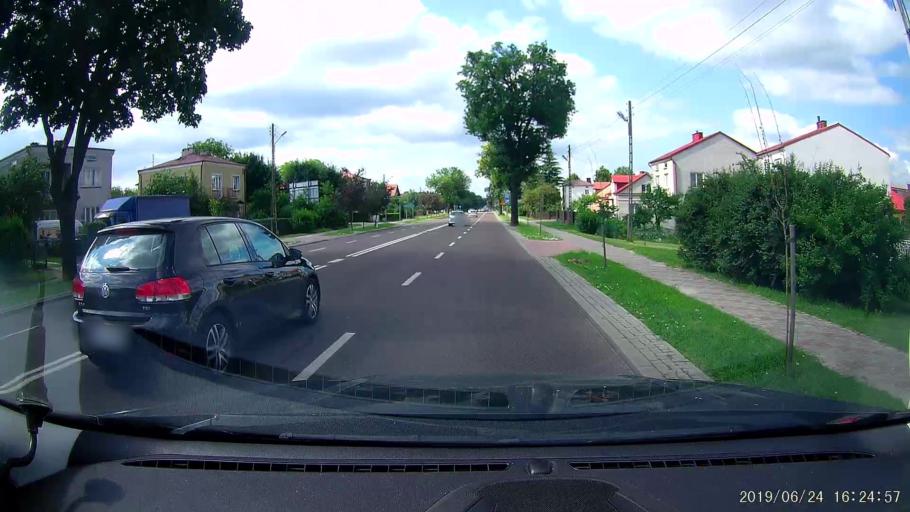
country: PL
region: Lublin Voivodeship
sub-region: Powiat tomaszowski
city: Tomaszow Lubelski
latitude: 50.4397
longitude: 23.4188
